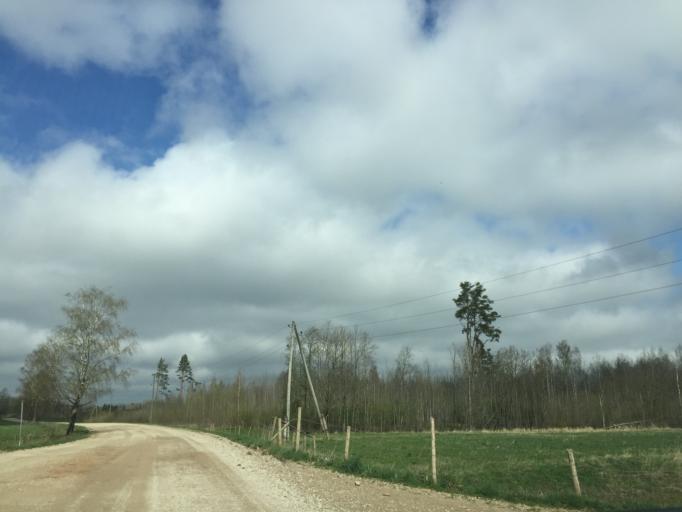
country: EE
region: Valgamaa
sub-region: Valga linn
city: Valga
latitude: 57.5566
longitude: 26.2816
